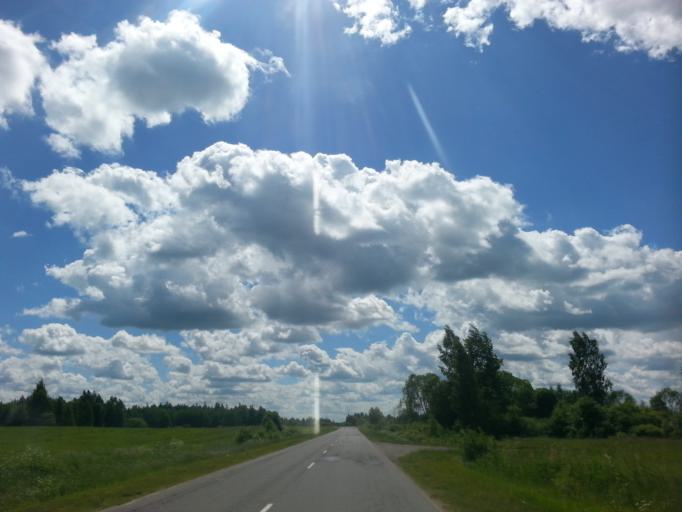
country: BY
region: Vitebsk
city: Mosar
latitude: 55.1541
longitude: 27.3394
